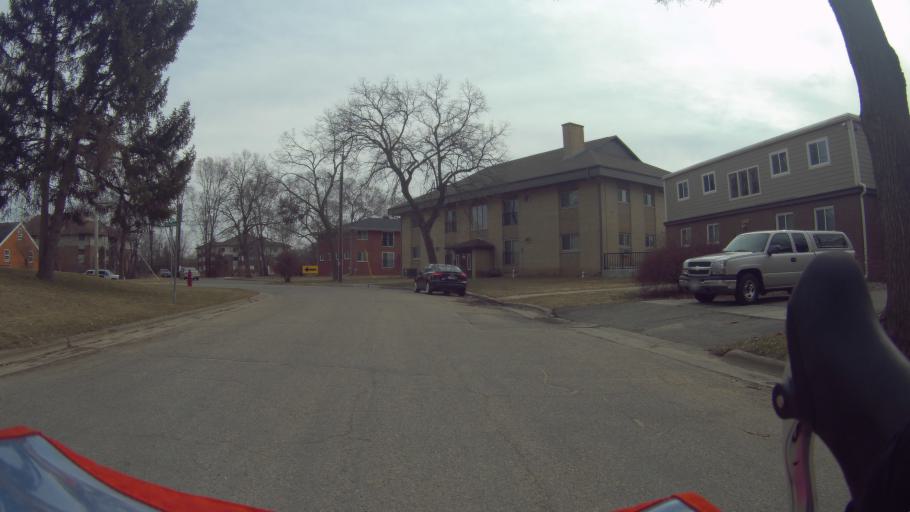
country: US
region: Wisconsin
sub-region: Dane County
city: Maple Bluff
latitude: 43.1154
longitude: -89.3661
